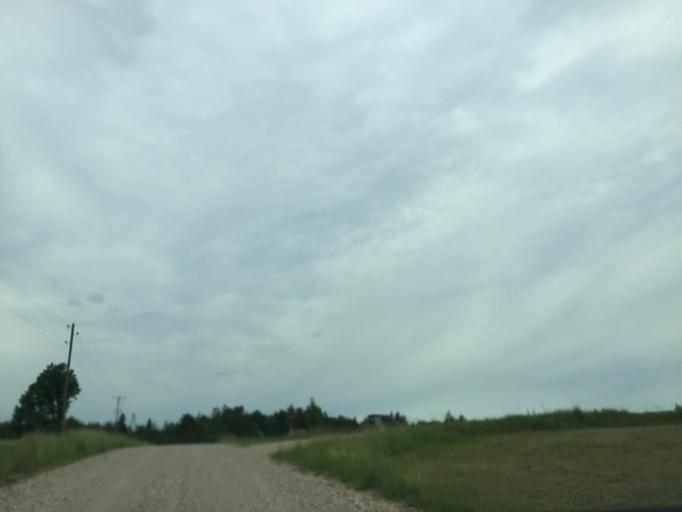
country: LV
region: Tukuma Rajons
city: Tukums
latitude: 57.0429
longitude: 23.1055
